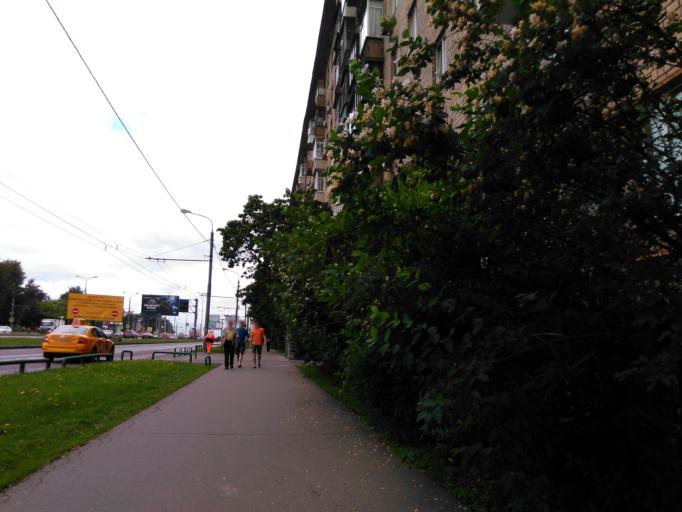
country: RU
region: Moskovskaya
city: Semenovskoye
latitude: 55.6904
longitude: 37.5318
